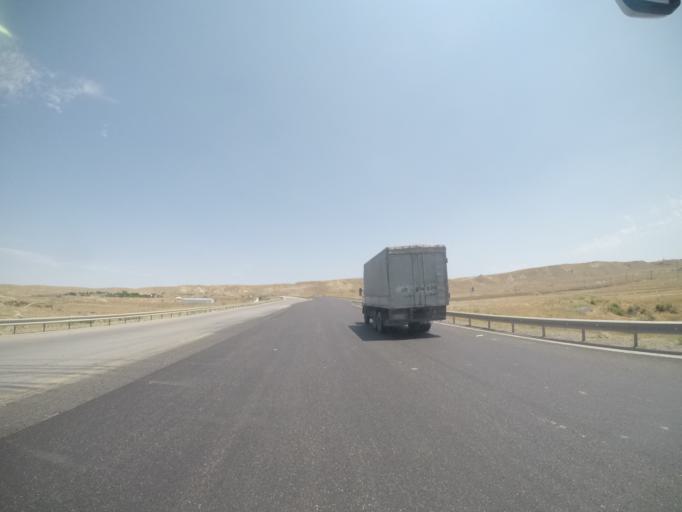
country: AZ
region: Haciqabul
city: Haciqabul
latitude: 40.0158
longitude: 48.9474
